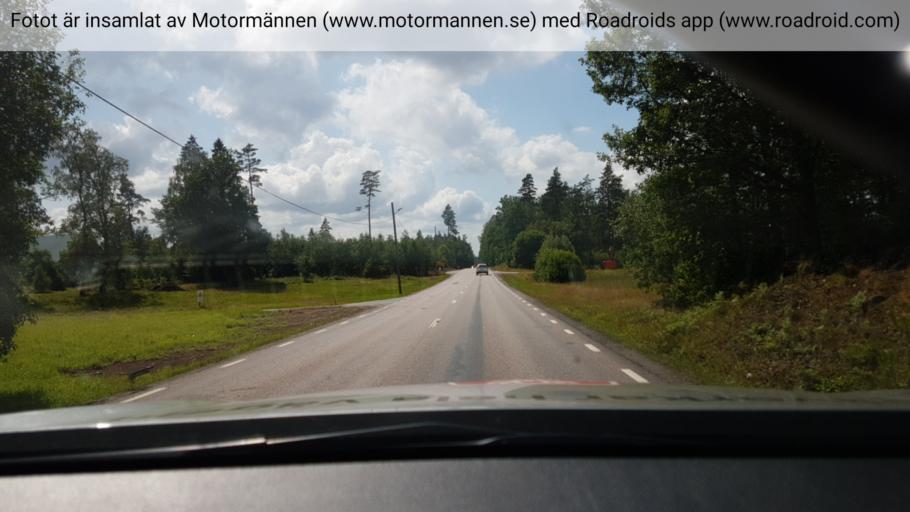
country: SE
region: Vaestra Goetaland
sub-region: Svenljunga Kommun
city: Svenljunga
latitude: 57.4966
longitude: 13.0850
